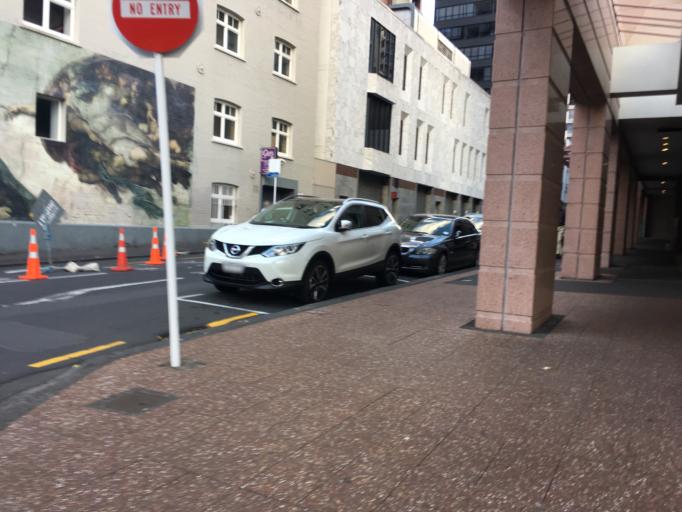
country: NZ
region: Auckland
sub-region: Auckland
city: Auckland
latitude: -36.8468
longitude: 174.7631
